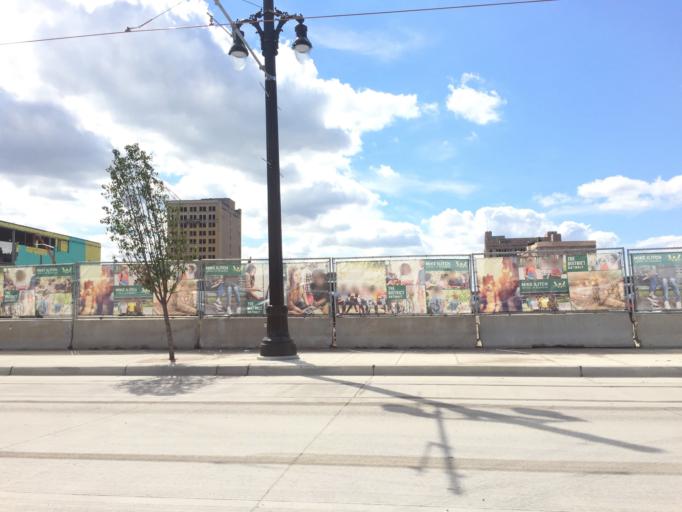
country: US
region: Michigan
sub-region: Wayne County
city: Detroit
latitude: 42.3431
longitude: -83.0551
